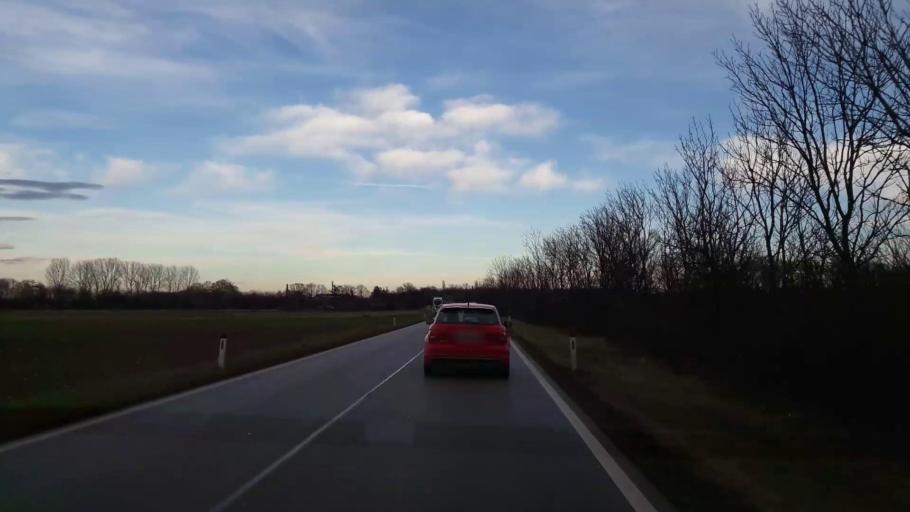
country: AT
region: Lower Austria
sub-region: Politischer Bezirk Baden
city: Ebreichsdorf
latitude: 47.9540
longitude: 16.4195
